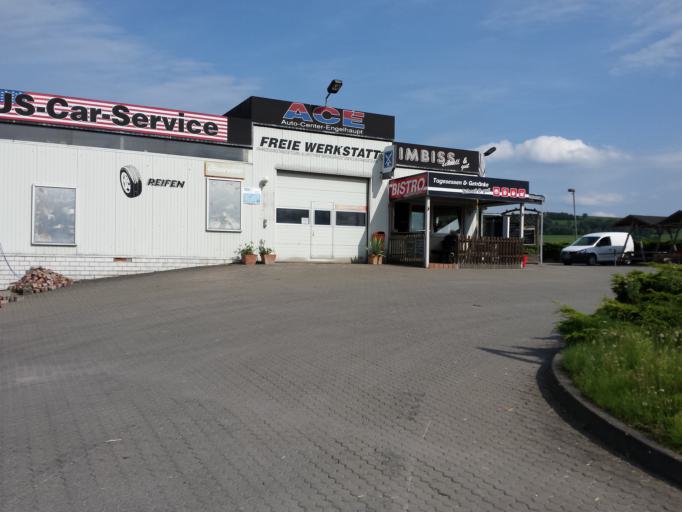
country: DE
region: Thuringia
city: Fambach
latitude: 50.7303
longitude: 10.3658
